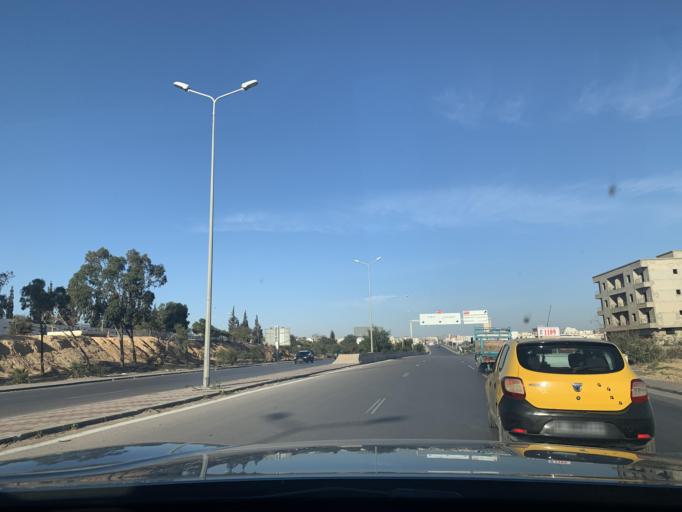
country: DZ
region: Souk Ahras
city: Souk Ahras
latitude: 36.3648
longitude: 8.0044
